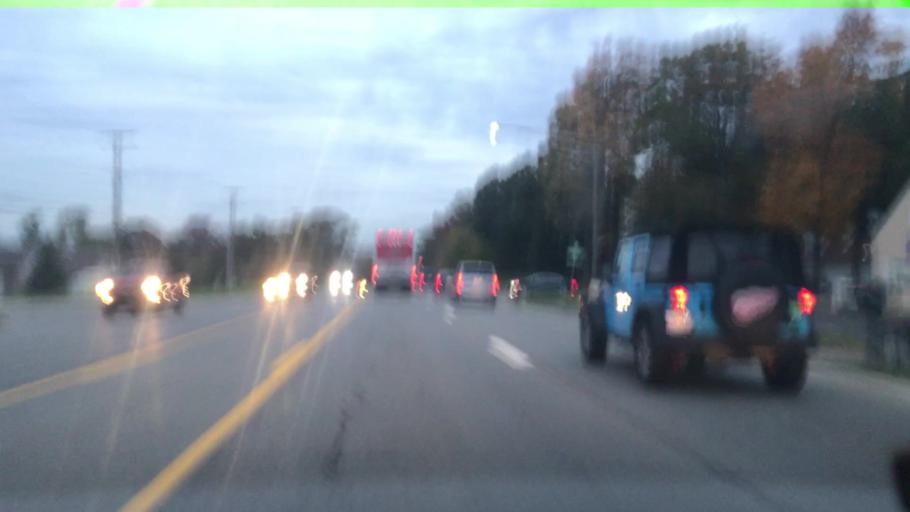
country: US
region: Michigan
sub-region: Oakland County
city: Pontiac
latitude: 42.6278
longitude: -83.2491
